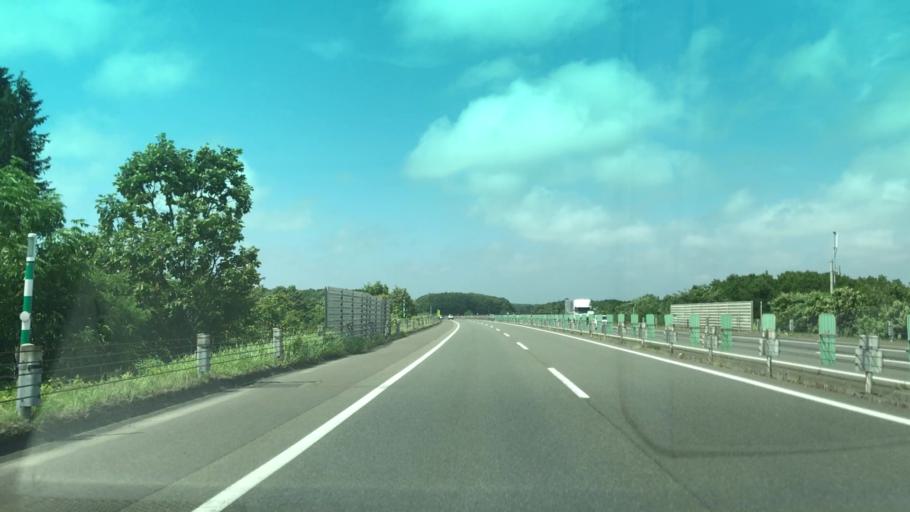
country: JP
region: Hokkaido
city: Kitahiroshima
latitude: 42.9116
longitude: 141.5495
